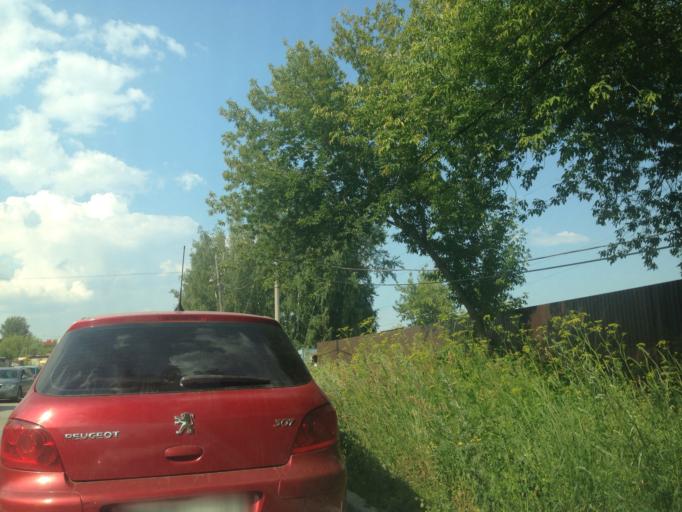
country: RU
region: Sverdlovsk
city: Yekaterinburg
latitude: 56.8676
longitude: 60.6375
